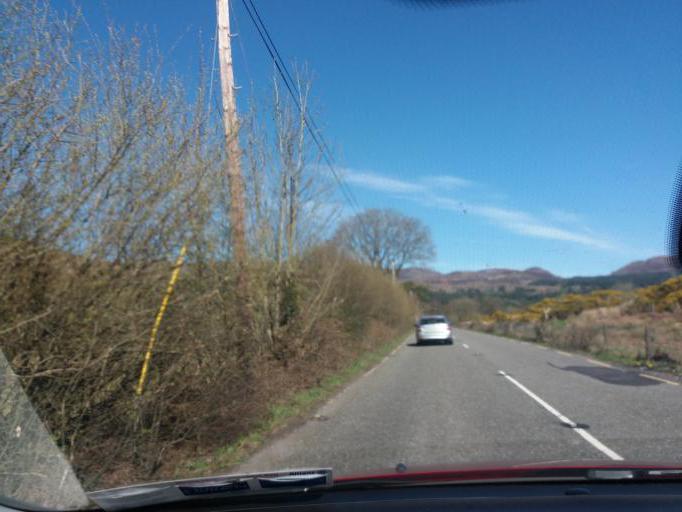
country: IE
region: Munster
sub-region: Ciarrai
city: Cill Airne
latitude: 51.9442
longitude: -9.3861
